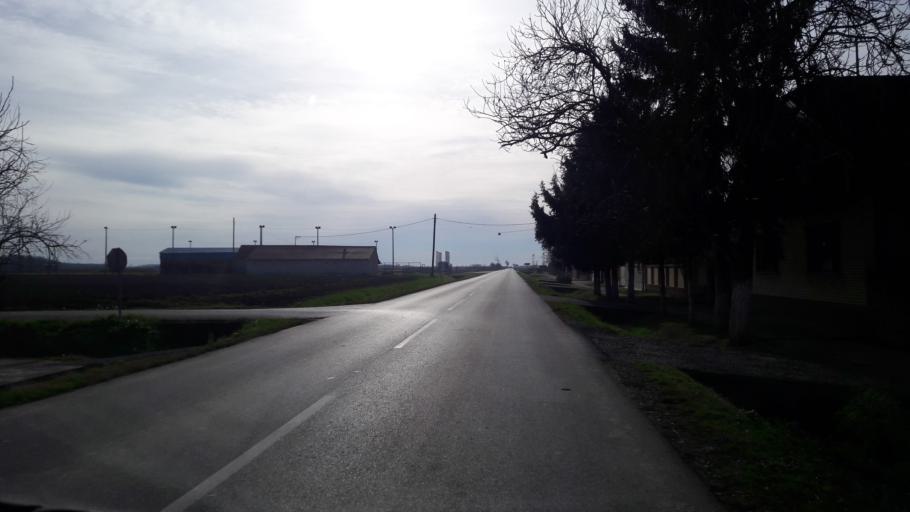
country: HR
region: Osjecko-Baranjska
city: Semeljci
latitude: 45.3446
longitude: 18.5575
